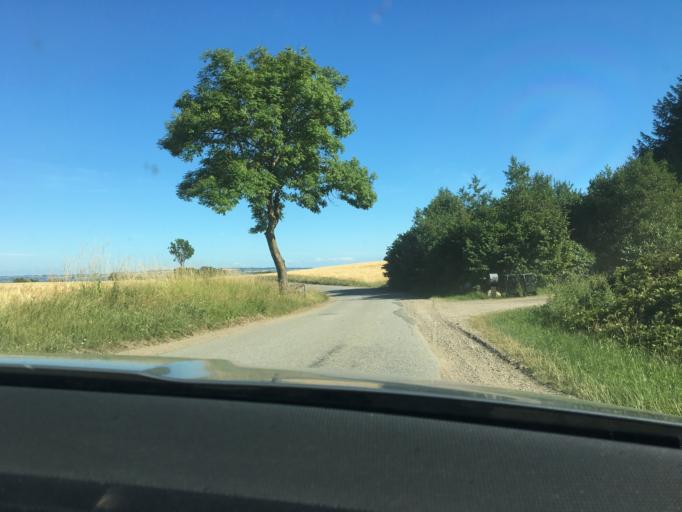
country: DK
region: Central Jutland
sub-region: Syddjurs Kommune
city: Hornslet
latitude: 56.2990
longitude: 10.3718
